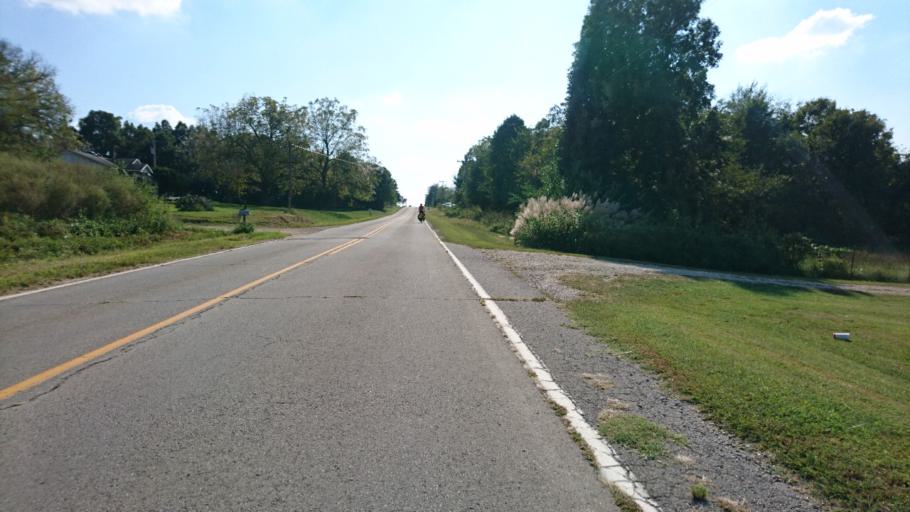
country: US
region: Missouri
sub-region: Laclede County
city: Lebanon
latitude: 37.6075
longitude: -92.7050
